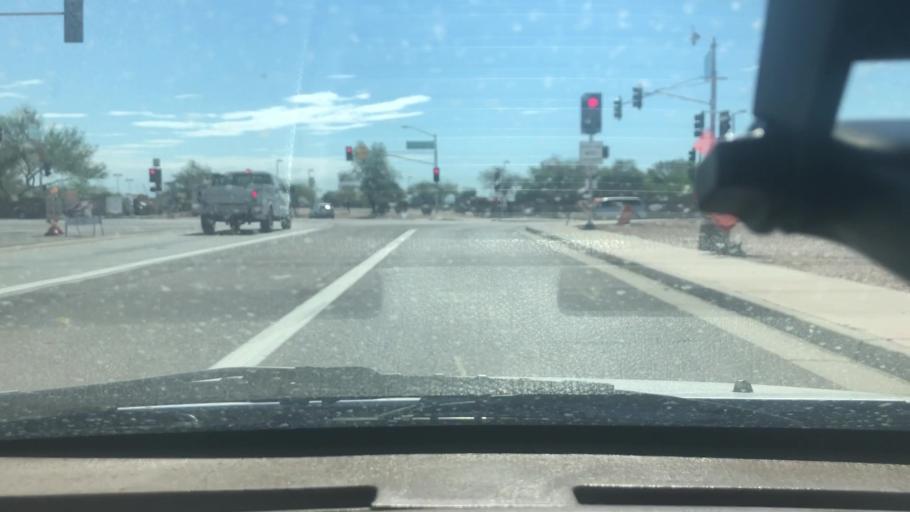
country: US
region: Arizona
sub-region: Maricopa County
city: Phoenix
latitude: 33.4305
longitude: -112.0349
